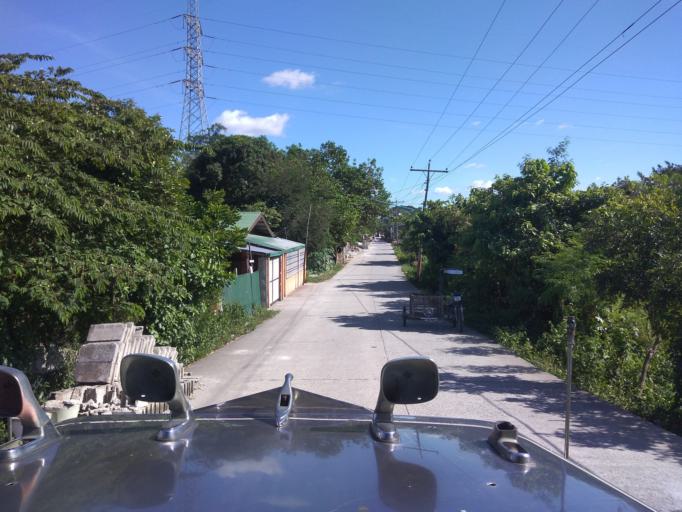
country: PH
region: Central Luzon
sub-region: Province of Pampanga
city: Bacolor
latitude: 15.0049
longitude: 120.6484
